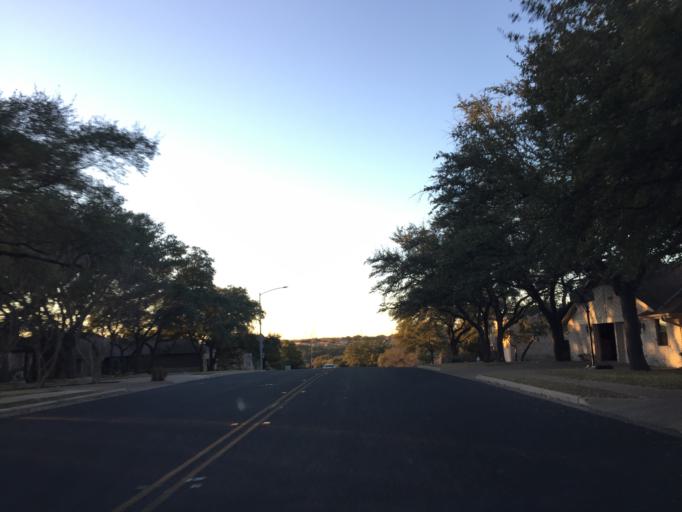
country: US
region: Texas
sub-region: Williamson County
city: Jollyville
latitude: 30.3965
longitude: -97.7565
